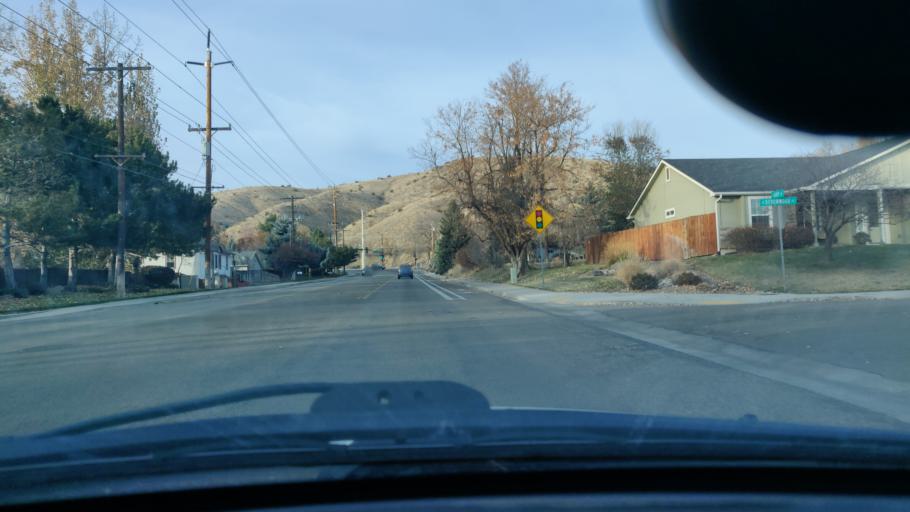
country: US
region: Idaho
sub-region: Ada County
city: Garden City
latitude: 43.6822
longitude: -116.2792
